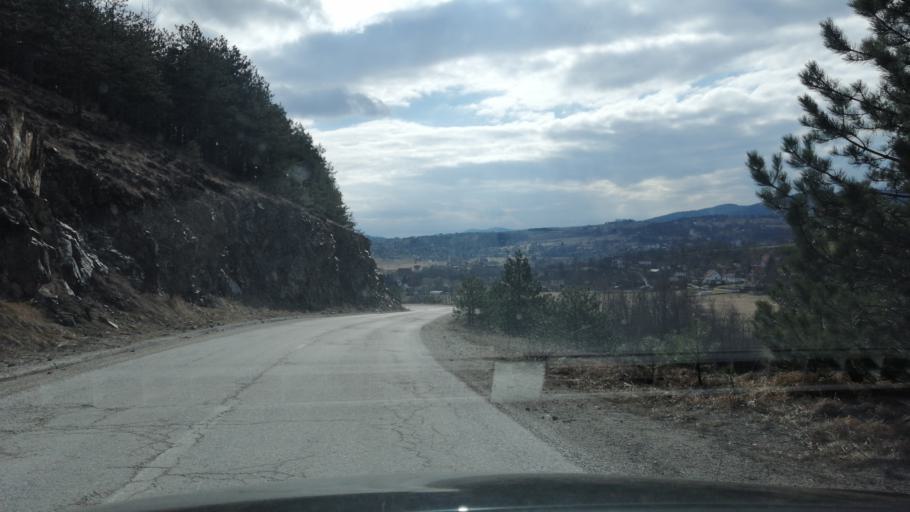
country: RS
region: Central Serbia
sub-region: Zlatiborski Okrug
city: Bajina Basta
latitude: 43.8616
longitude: 19.5782
